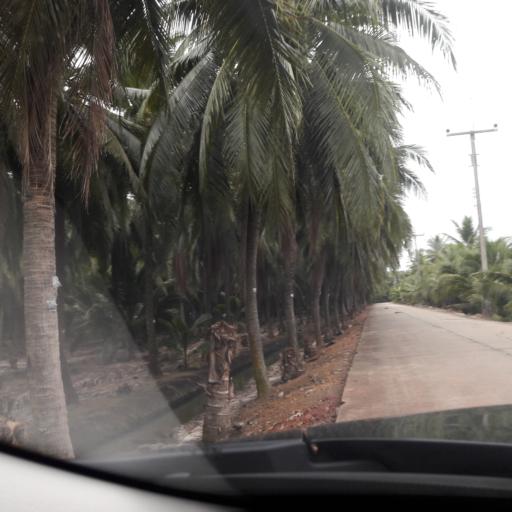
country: TH
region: Ratchaburi
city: Damnoen Saduak
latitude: 13.5797
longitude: 99.9464
